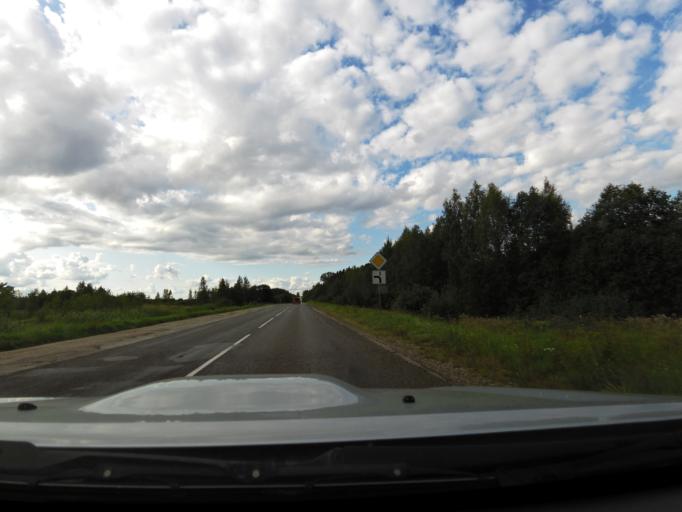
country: LV
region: Akniste
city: Akniste
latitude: 56.0215
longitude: 25.9212
